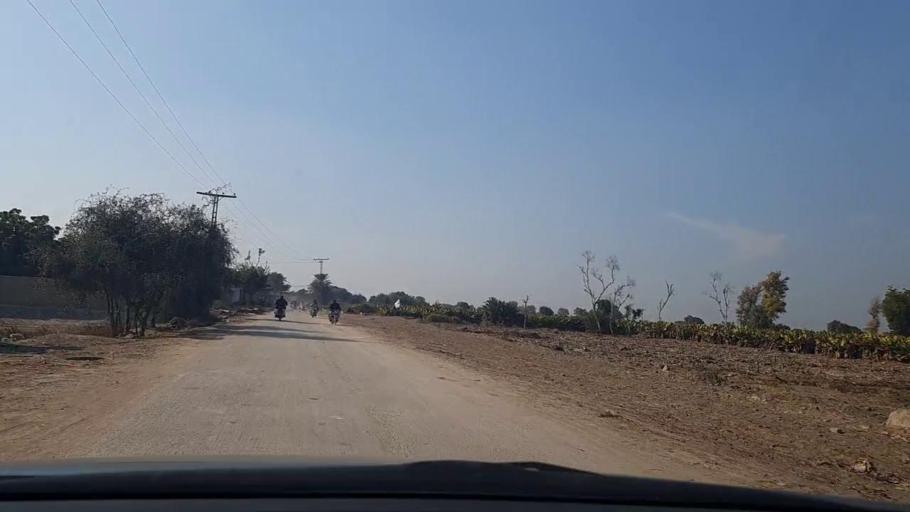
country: PK
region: Sindh
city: Daulatpur
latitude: 26.3043
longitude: 68.0913
